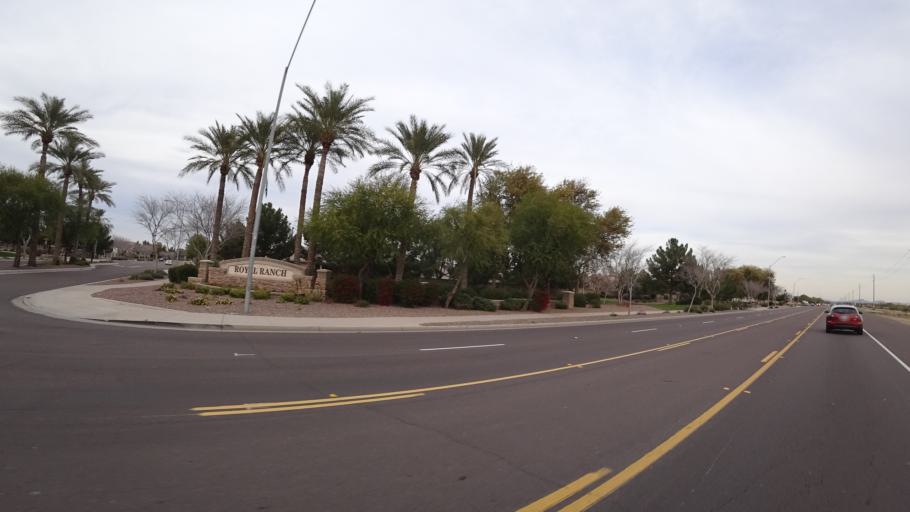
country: US
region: Arizona
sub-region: Maricopa County
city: Surprise
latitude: 33.6092
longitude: -112.3725
